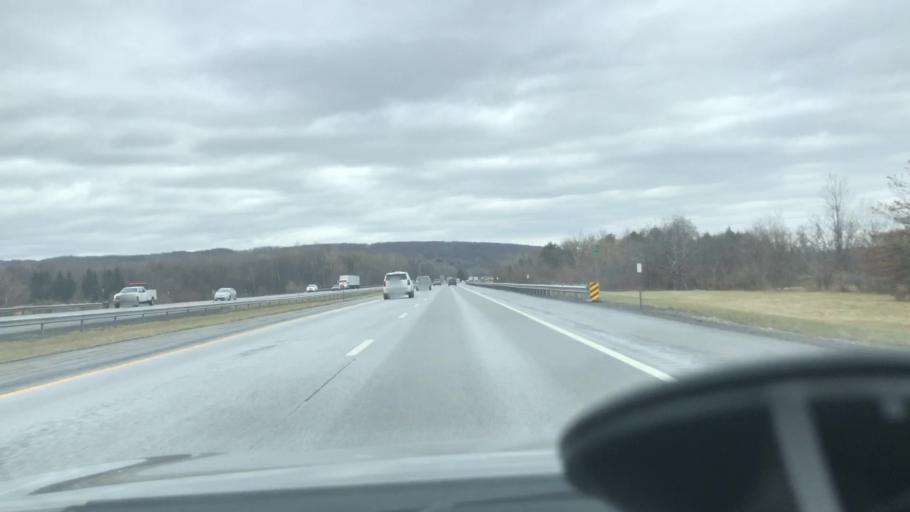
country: US
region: New York
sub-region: Herkimer County
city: Frankfort
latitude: 43.0613
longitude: -75.0773
